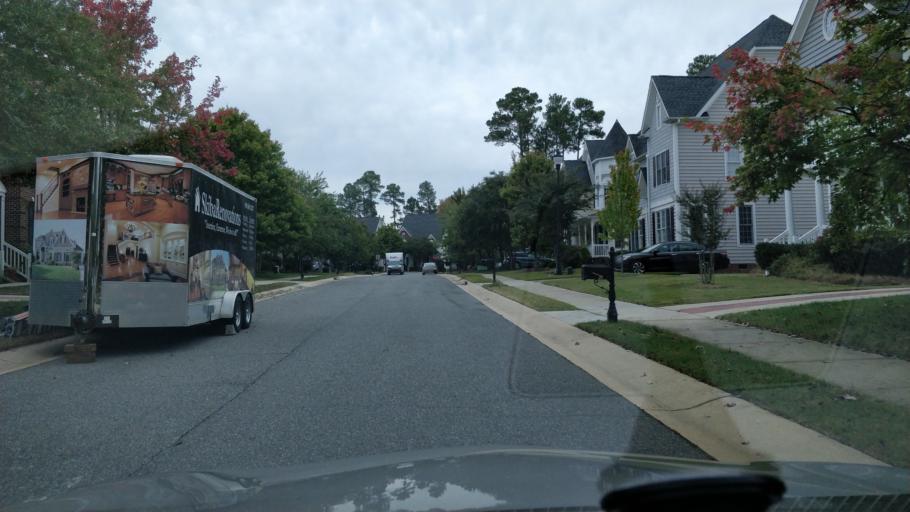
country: US
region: North Carolina
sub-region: Wake County
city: Morrisville
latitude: 35.8206
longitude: -78.8340
